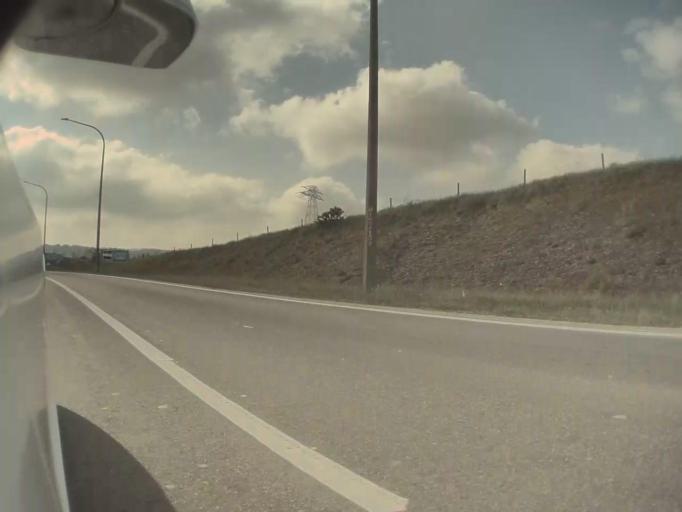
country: BE
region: Wallonia
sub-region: Province du Luxembourg
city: Marche-en-Famenne
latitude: 50.2386
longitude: 5.3408
